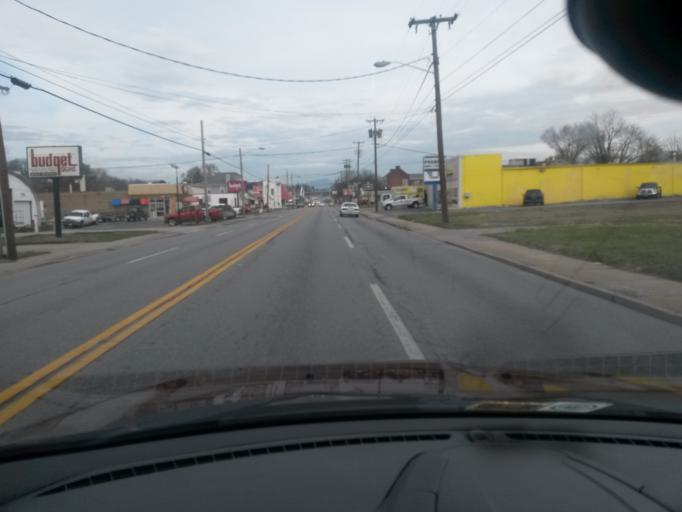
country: US
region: Virginia
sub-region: City of Roanoke
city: Roanoke
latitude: 37.2991
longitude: -79.9404
